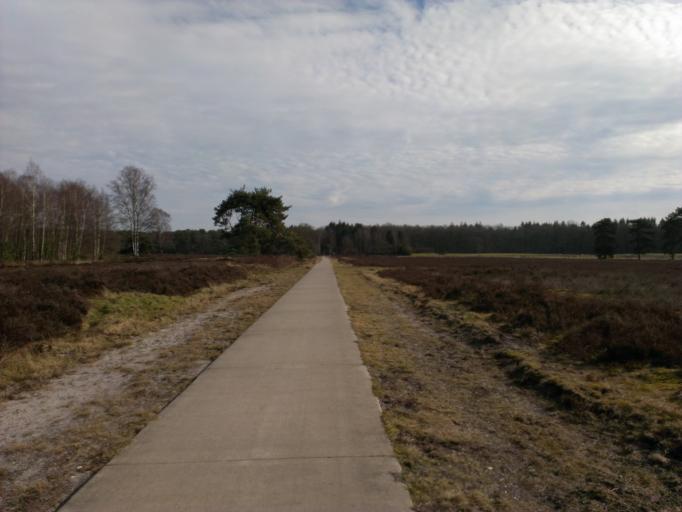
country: NL
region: Gelderland
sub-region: Gemeente Epe
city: Epe
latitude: 52.3885
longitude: 5.9895
